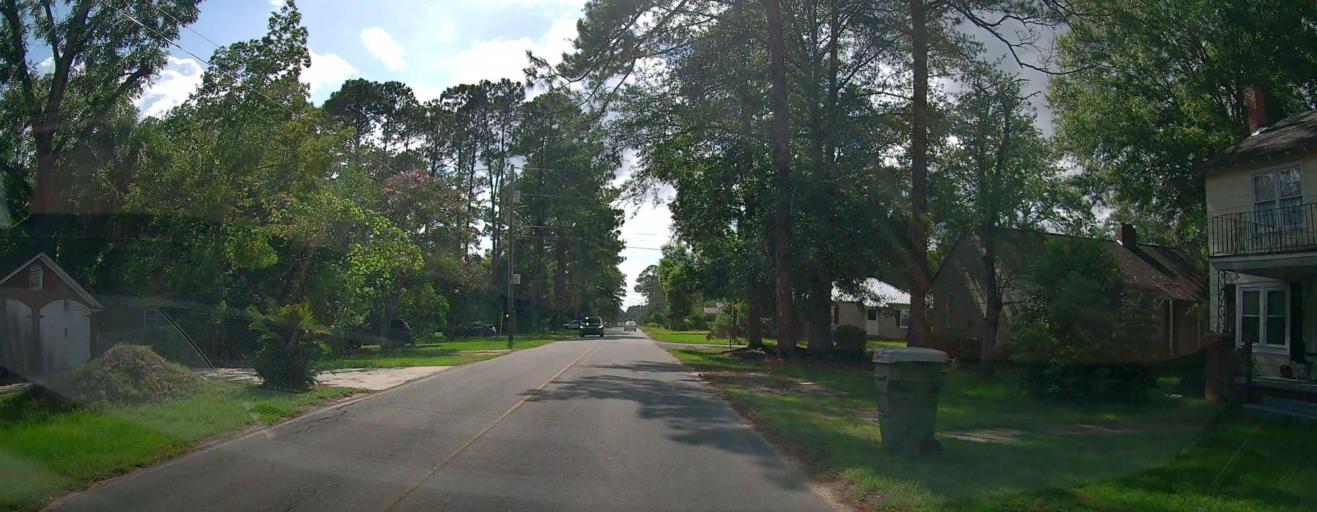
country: US
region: Georgia
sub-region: Coffee County
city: Douglas
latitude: 31.5170
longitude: -82.8452
